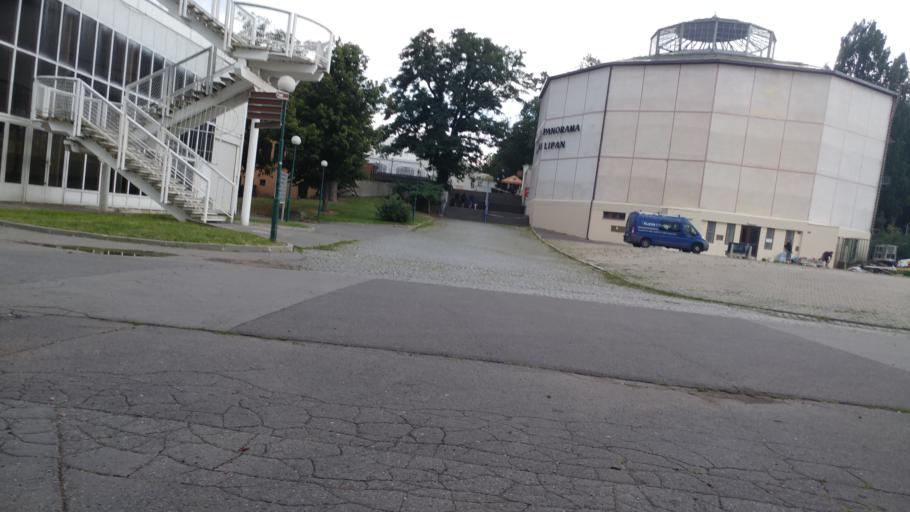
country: CZ
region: Praha
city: Prague
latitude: 50.1073
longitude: 14.4274
